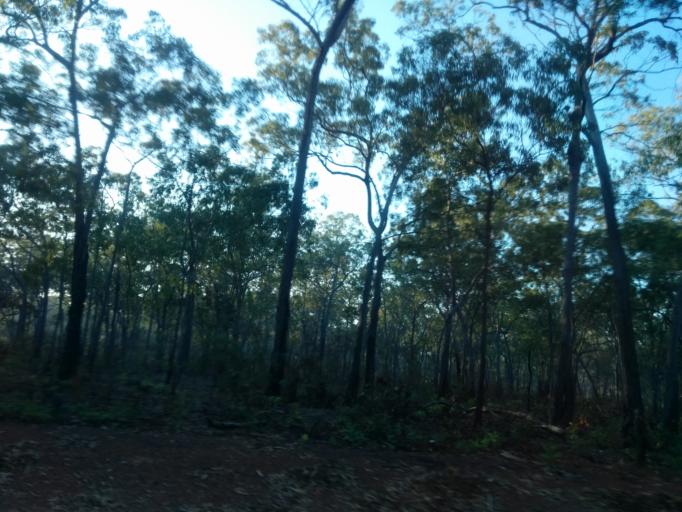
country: AU
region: Northern Territory
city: Alyangula
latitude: -13.8637
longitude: 136.8076
